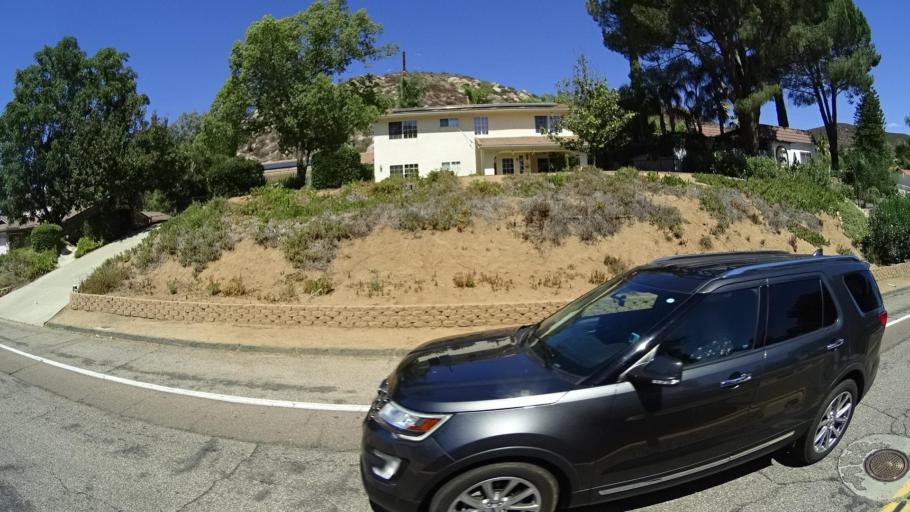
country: US
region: California
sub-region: San Diego County
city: San Diego Country Estates
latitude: 33.0267
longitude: -116.8138
